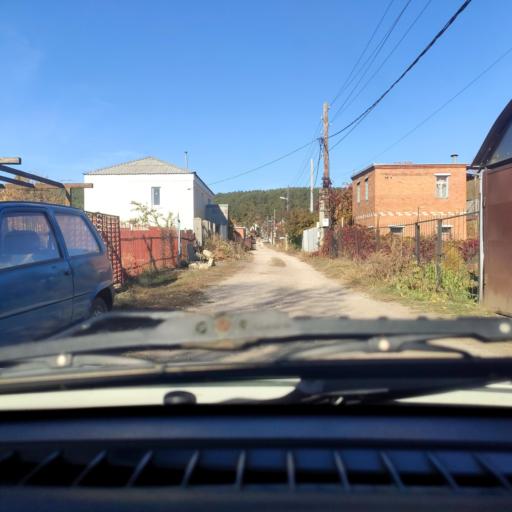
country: RU
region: Samara
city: Zhigulevsk
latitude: 53.4664
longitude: 49.5882
